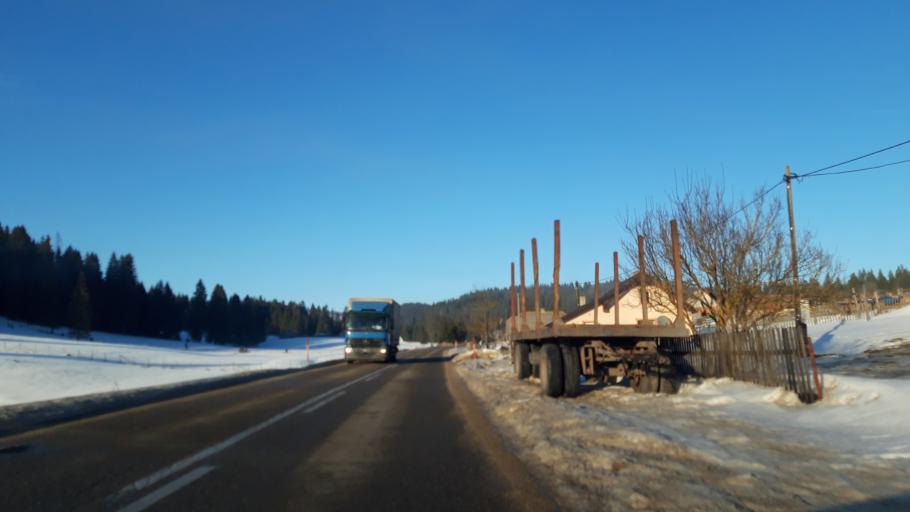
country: BA
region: Republika Srpska
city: Han Pijesak
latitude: 44.1107
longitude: 18.9684
